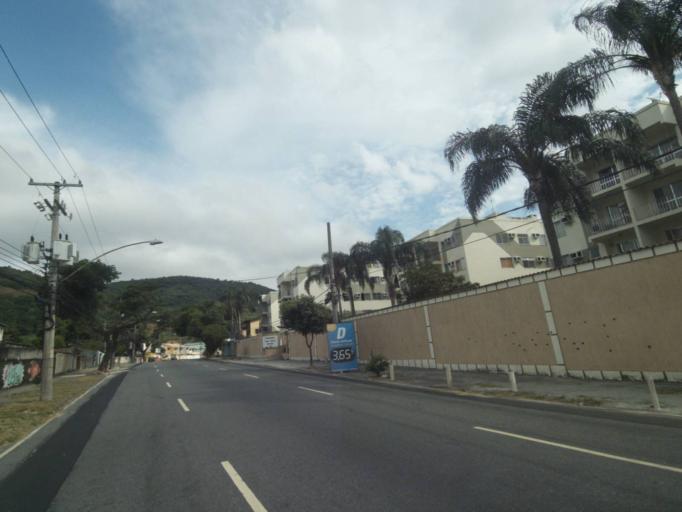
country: BR
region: Rio de Janeiro
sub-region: Nilopolis
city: Nilopolis
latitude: -22.8891
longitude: -43.3944
